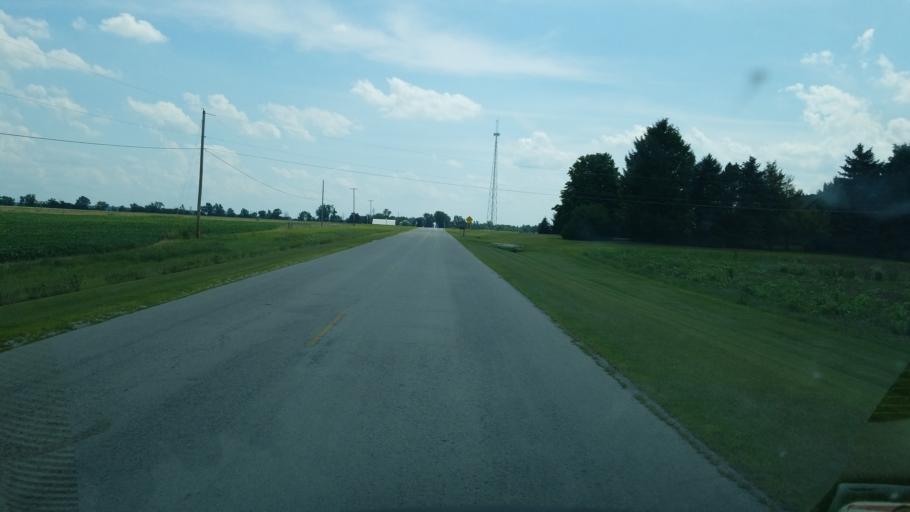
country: US
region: Ohio
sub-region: Hardin County
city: Forest
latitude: 40.8292
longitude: -83.4774
